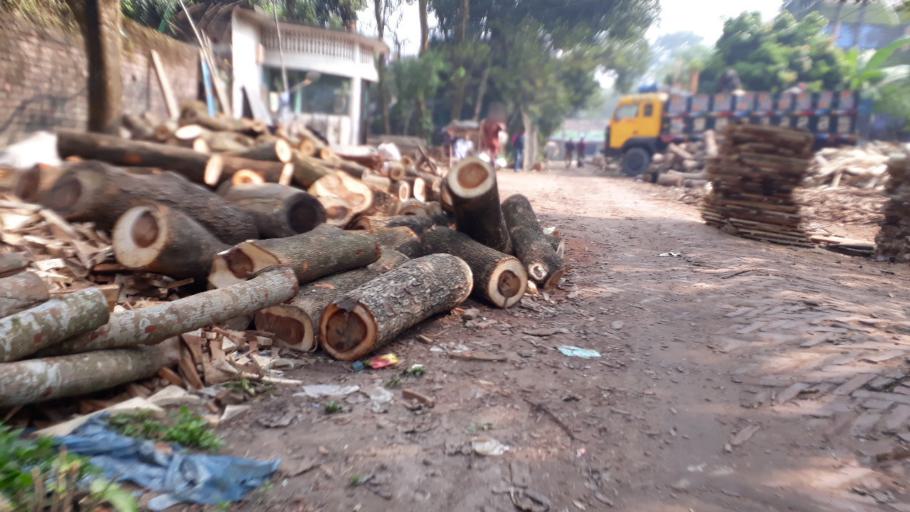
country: BD
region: Khulna
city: Kaliganj
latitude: 23.3539
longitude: 88.9141
